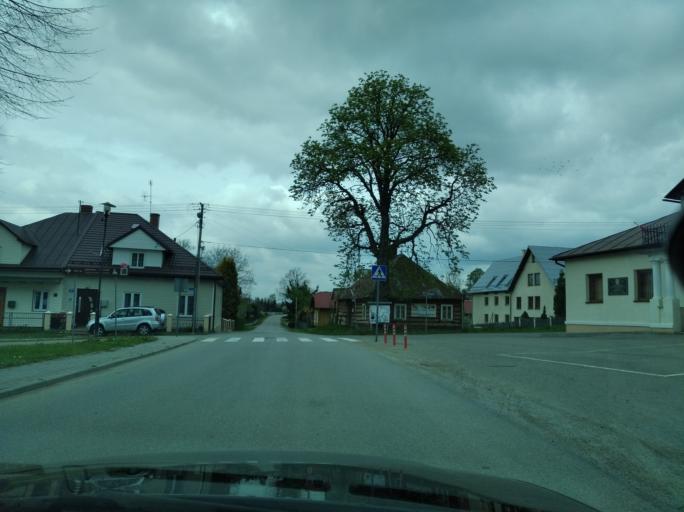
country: PL
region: Subcarpathian Voivodeship
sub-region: Powiat brzozowski
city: Gorki
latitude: 49.6204
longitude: 22.0190
